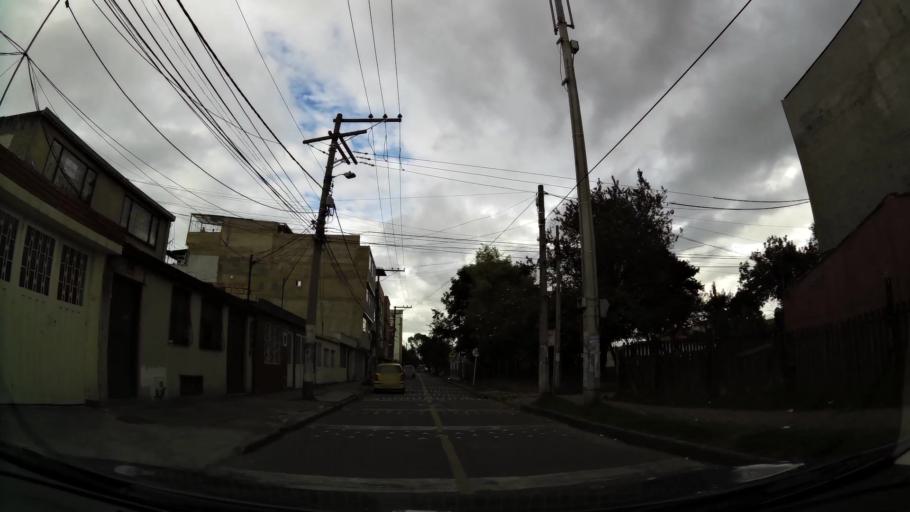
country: CO
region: Bogota D.C.
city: Barrio San Luis
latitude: 4.7050
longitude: -74.1105
